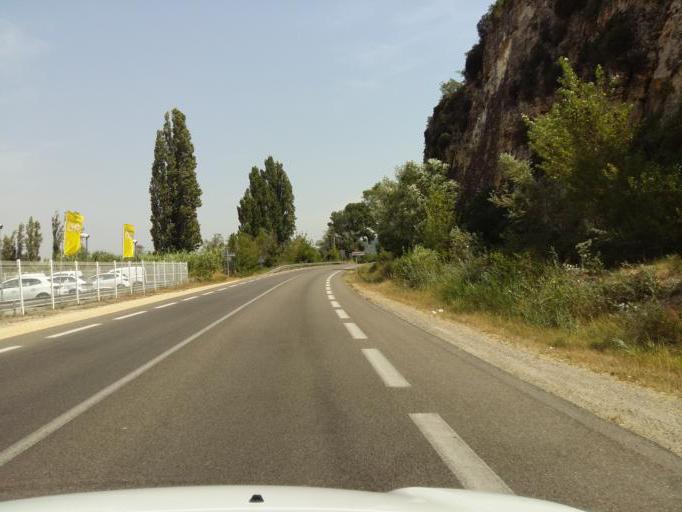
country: FR
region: Provence-Alpes-Cote d'Azur
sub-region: Departement du Vaucluse
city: Mondragon
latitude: 44.2427
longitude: 4.7171
